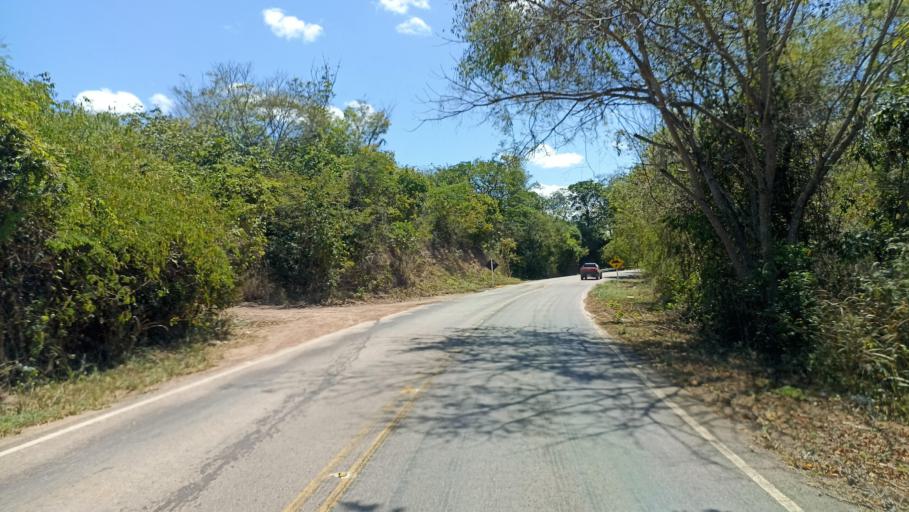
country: BR
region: Bahia
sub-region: Andarai
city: Vera Cruz
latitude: -12.7582
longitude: -41.3287
